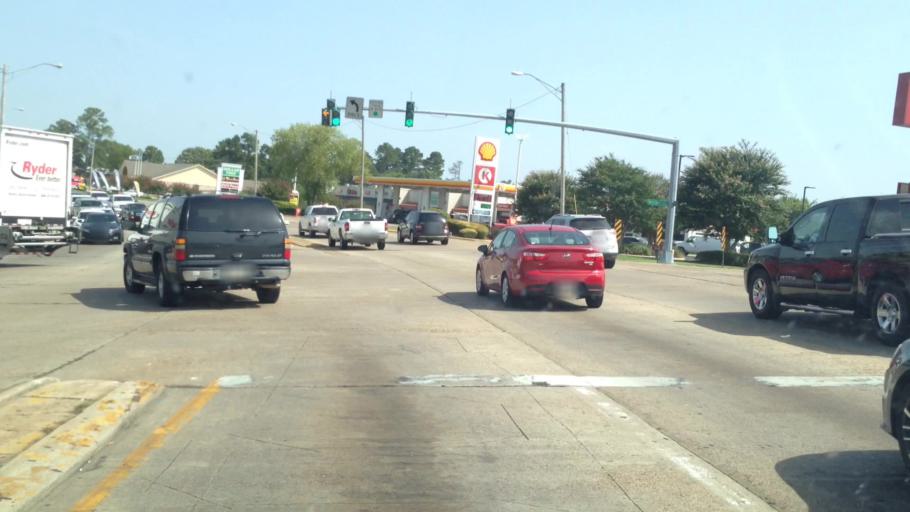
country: US
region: Louisiana
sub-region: Caddo Parish
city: Greenwood
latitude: 32.4485
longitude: -93.8655
